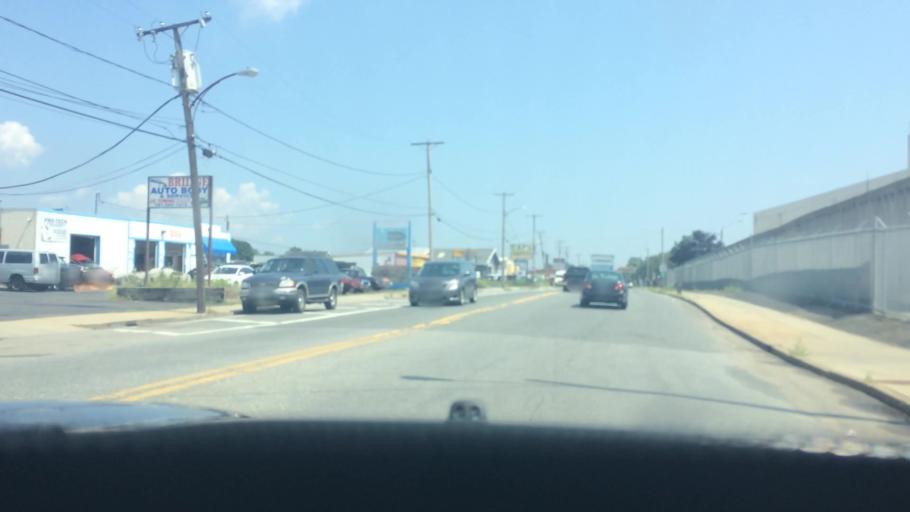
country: US
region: Massachusetts
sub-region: Essex County
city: Lynn
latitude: 42.4516
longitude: -70.9782
